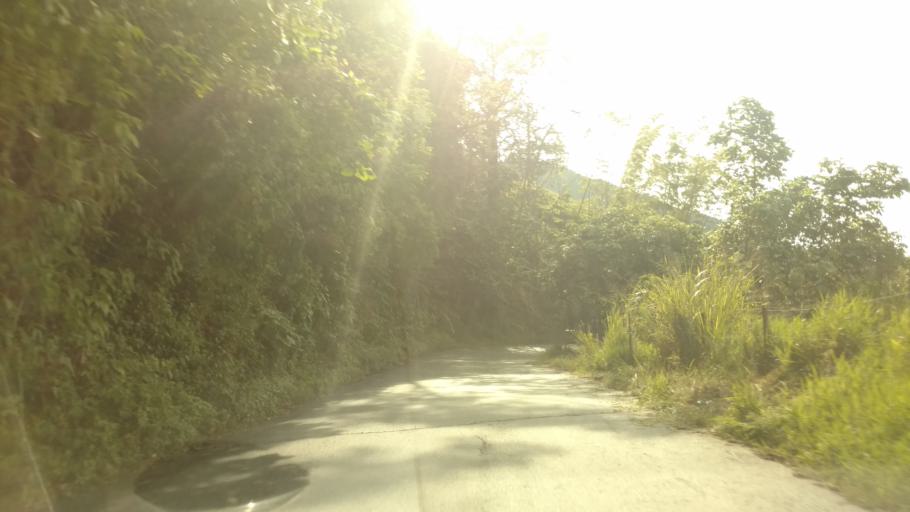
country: CO
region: Caldas
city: Neira
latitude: 5.1798
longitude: -75.5227
